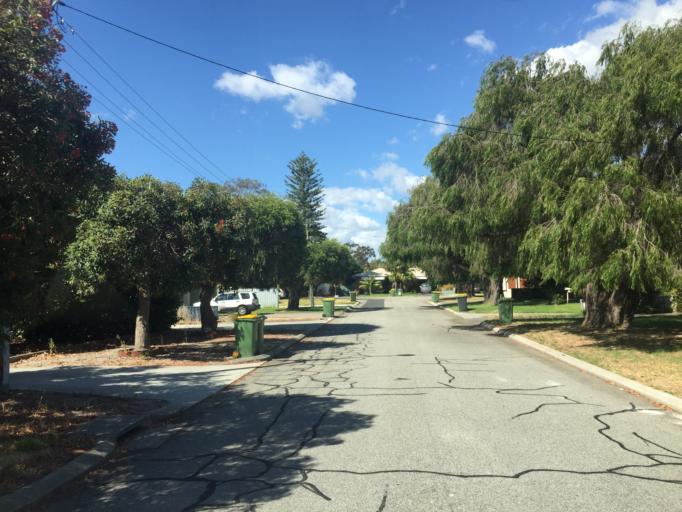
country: AU
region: Western Australia
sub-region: Belmont
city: Belmont
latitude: -31.9444
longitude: 115.9338
